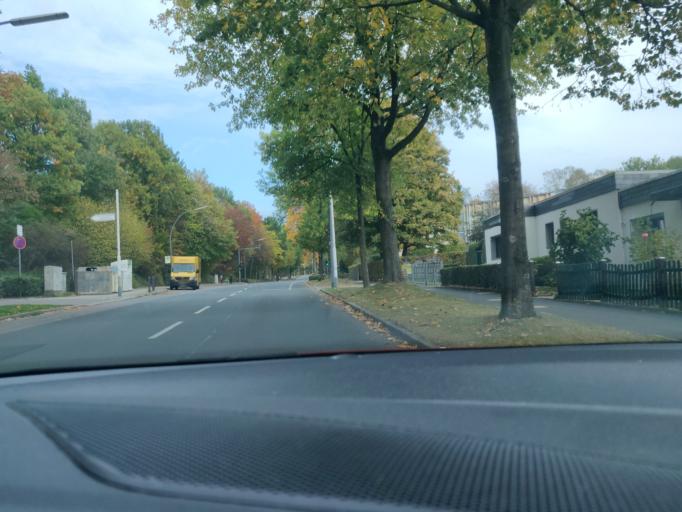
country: DE
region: North Rhine-Westphalia
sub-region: Regierungsbezirk Dusseldorf
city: Velbert
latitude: 51.3413
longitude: 7.0167
